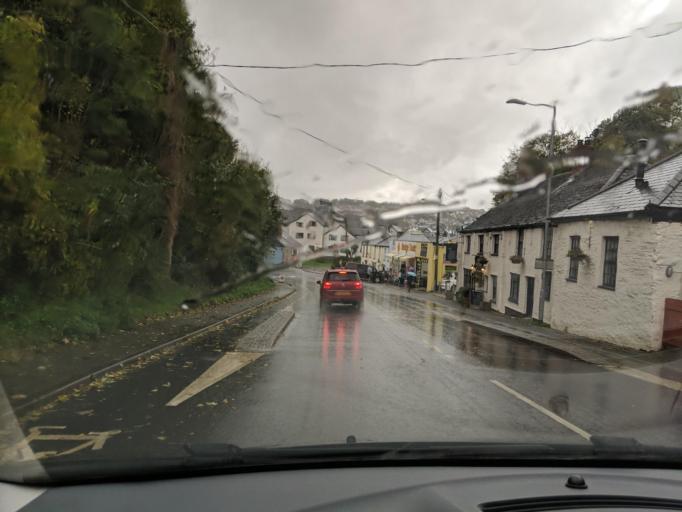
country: GB
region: England
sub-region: Cornwall
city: Wadebridge
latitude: 50.5193
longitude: -4.8333
